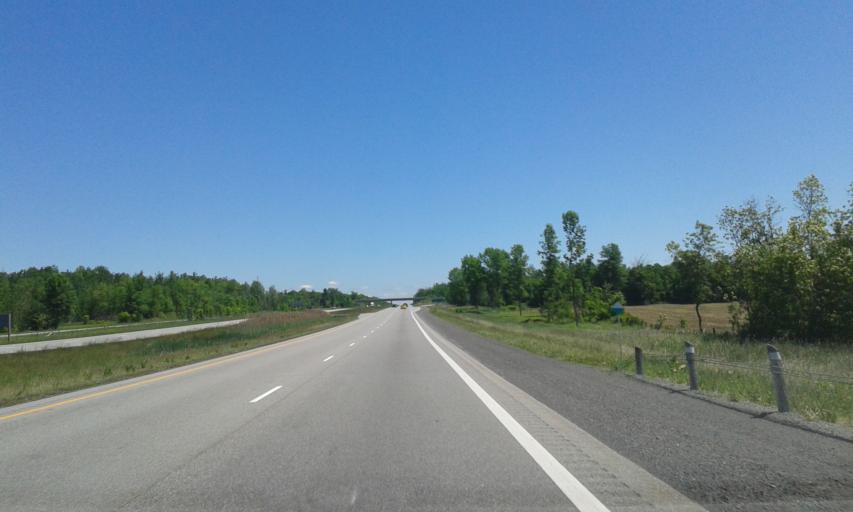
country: US
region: New York
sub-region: St. Lawrence County
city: Ogdensburg
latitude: 44.8053
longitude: -75.4136
